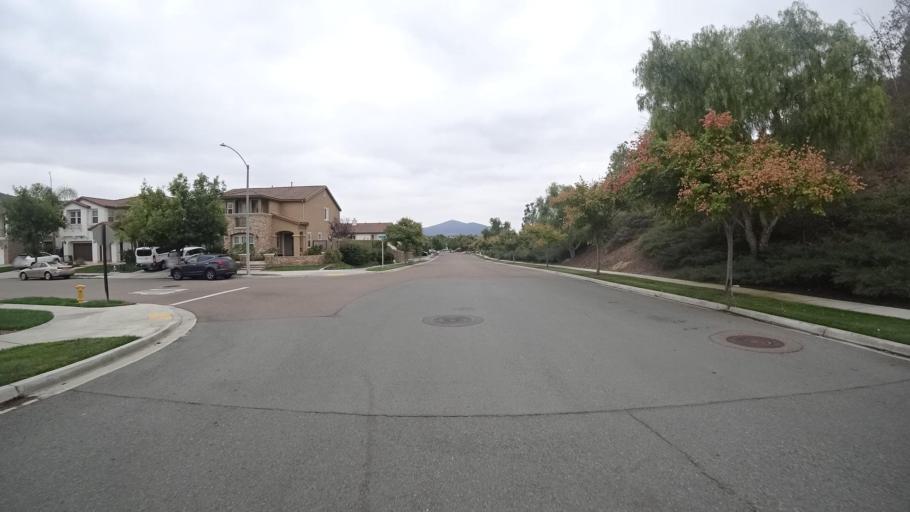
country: US
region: California
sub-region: San Diego County
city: Fairbanks Ranch
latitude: 33.0326
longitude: -117.1130
